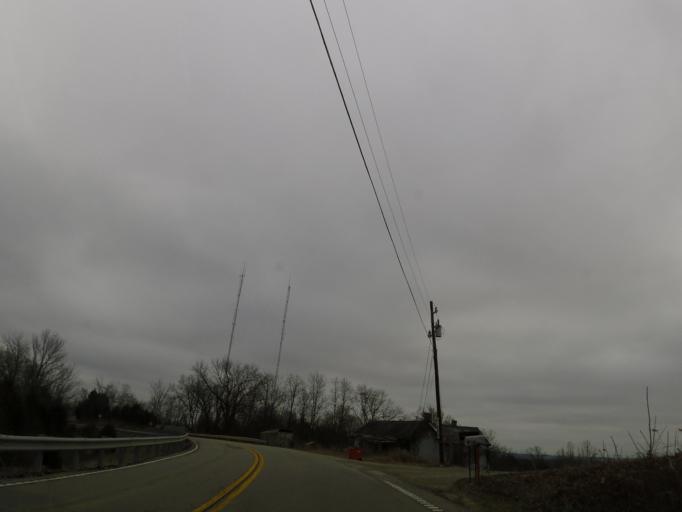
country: US
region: Kentucky
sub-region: Franklin County
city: Frankfort
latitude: 38.2177
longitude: -84.9086
